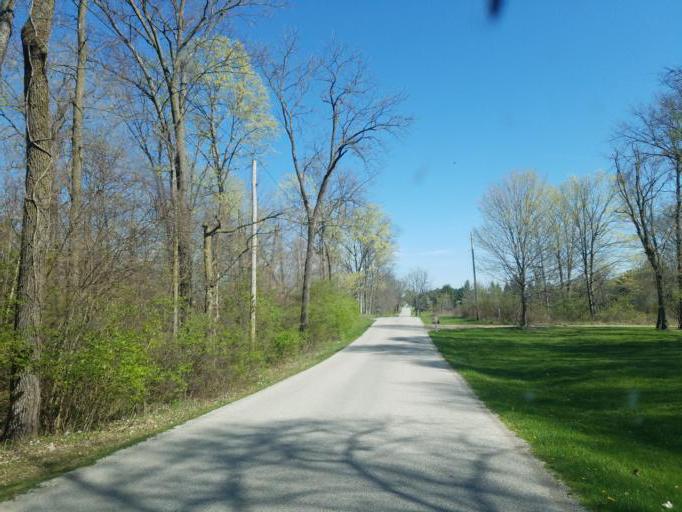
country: US
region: Ohio
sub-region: Morrow County
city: Mount Gilead
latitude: 40.5538
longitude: -82.7965
